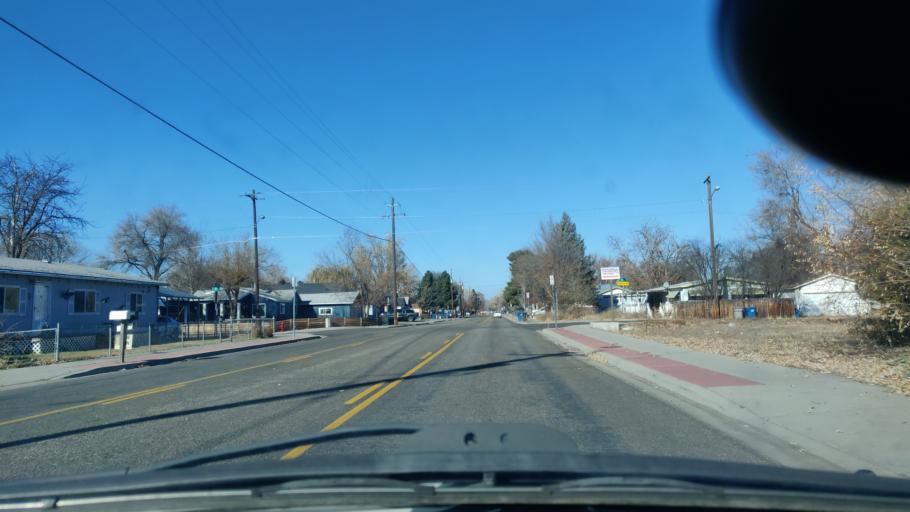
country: US
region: Idaho
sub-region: Ada County
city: Garden City
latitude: 43.6404
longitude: -116.2554
